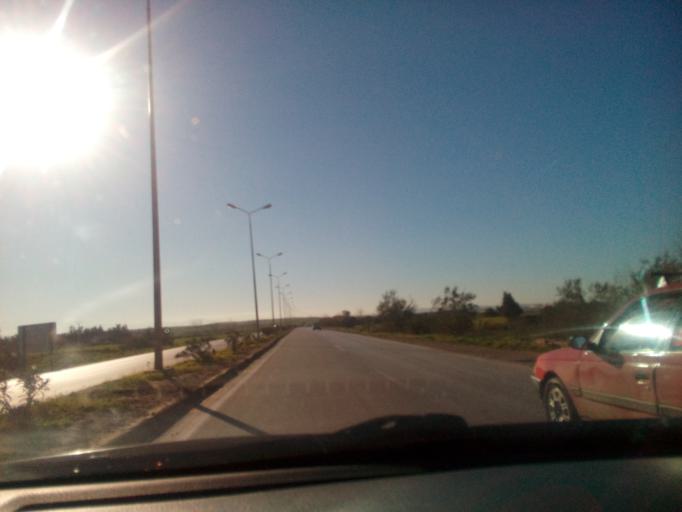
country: DZ
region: Relizane
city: Relizane
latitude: 35.7146
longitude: 0.5616
